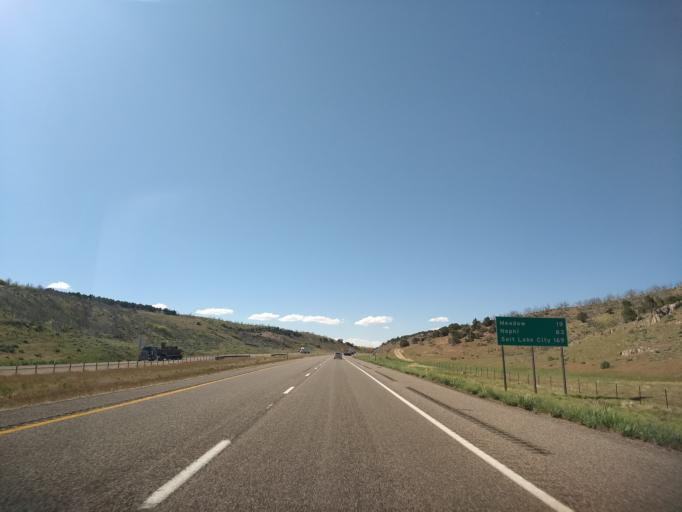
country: US
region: Utah
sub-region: Millard County
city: Fillmore
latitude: 38.6751
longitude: -112.5913
